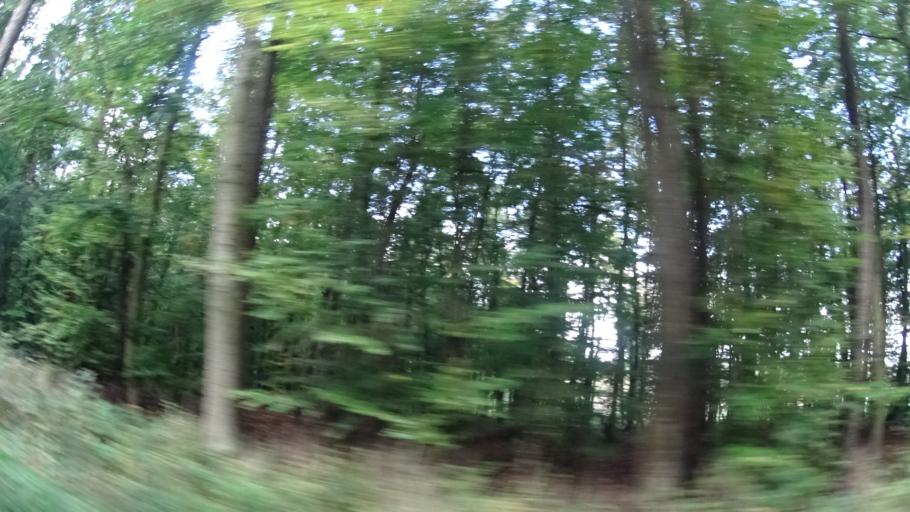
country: DE
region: Bavaria
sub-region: Regierungsbezirk Unterfranken
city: Frankenwinheim
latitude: 49.8637
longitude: 10.2795
